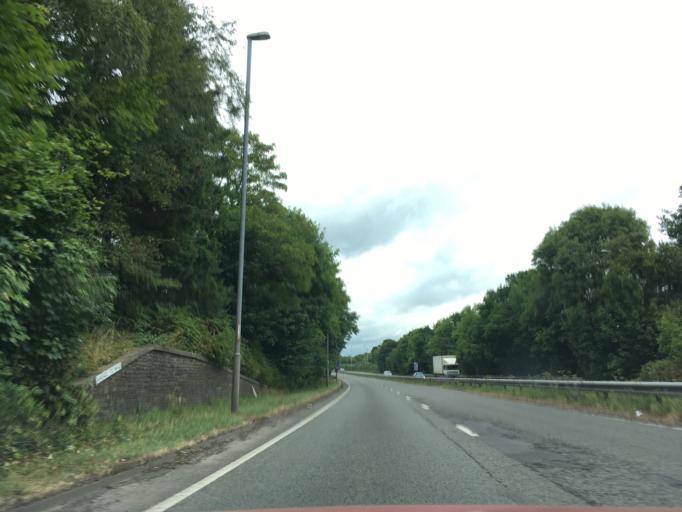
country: GB
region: Wales
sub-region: Torfaen County Borough
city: Cwmbran
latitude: 51.6577
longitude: -2.9990
